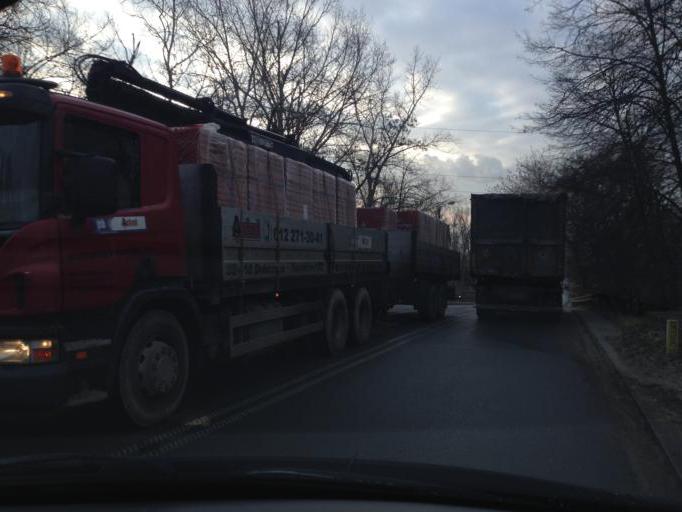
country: PL
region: Lesser Poland Voivodeship
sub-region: Powiat wielicki
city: Kokotow
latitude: 50.0643
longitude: 20.0815
